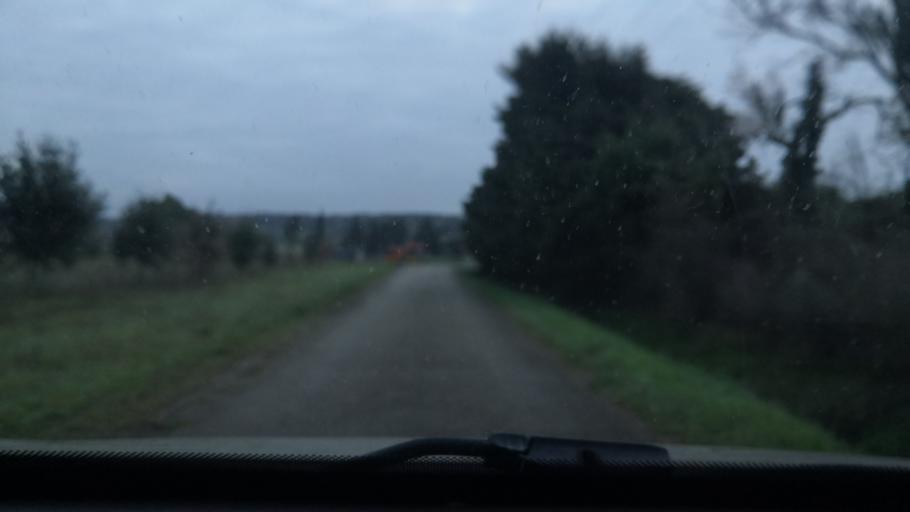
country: FR
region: Rhone-Alpes
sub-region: Departement de la Drome
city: Montelimar
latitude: 44.5273
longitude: 4.7519
